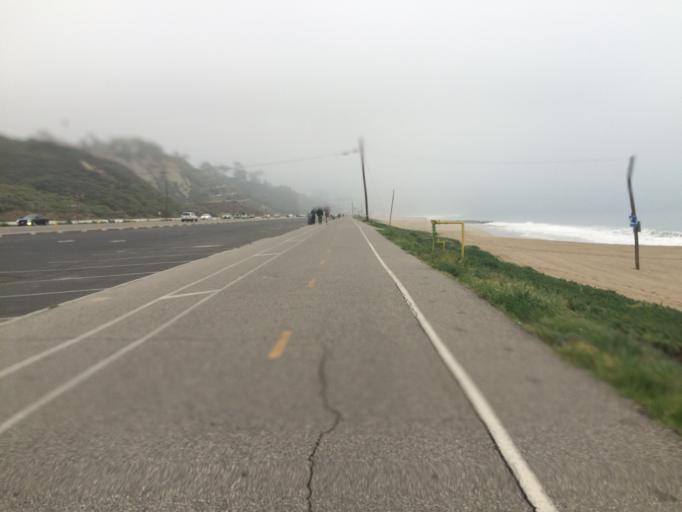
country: US
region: California
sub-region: Los Angeles County
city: Santa Monica
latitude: 34.0344
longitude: -118.5341
